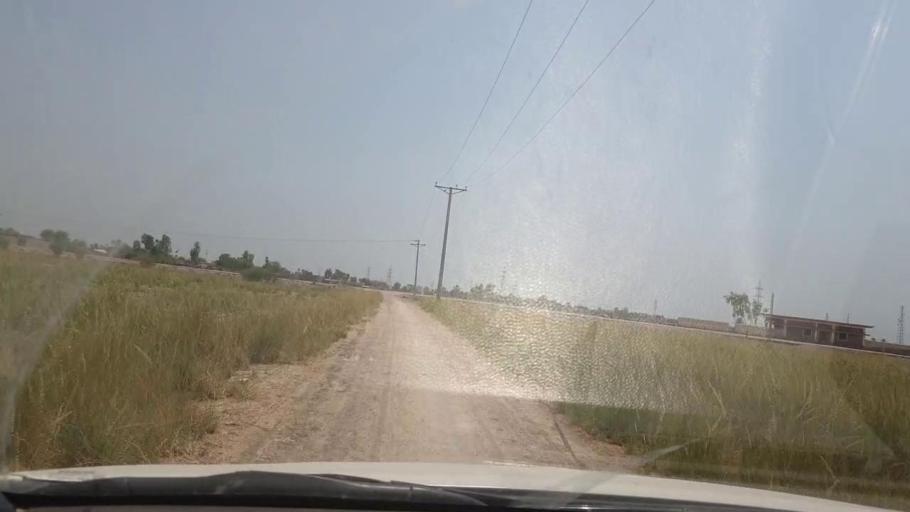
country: PK
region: Sindh
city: Lakhi
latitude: 27.8616
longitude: 68.7021
